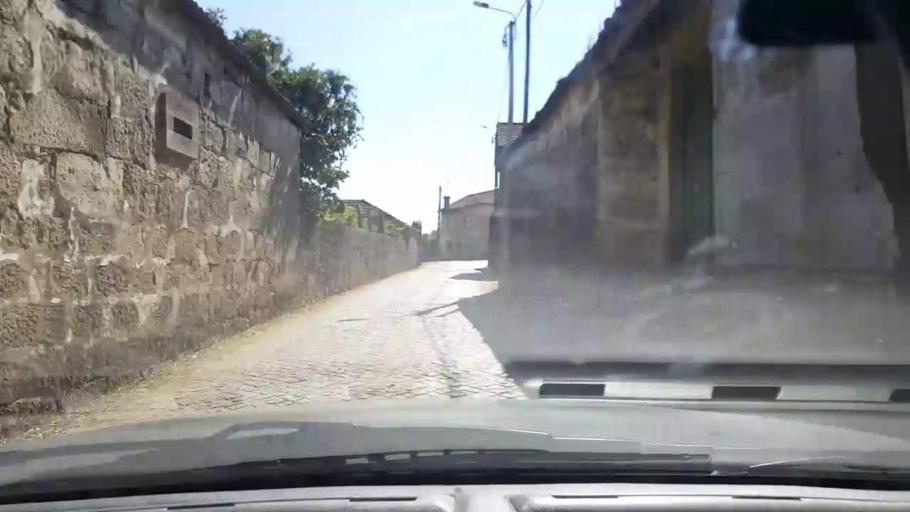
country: PT
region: Porto
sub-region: Matosinhos
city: Lavra
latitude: 41.2894
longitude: -8.6907
